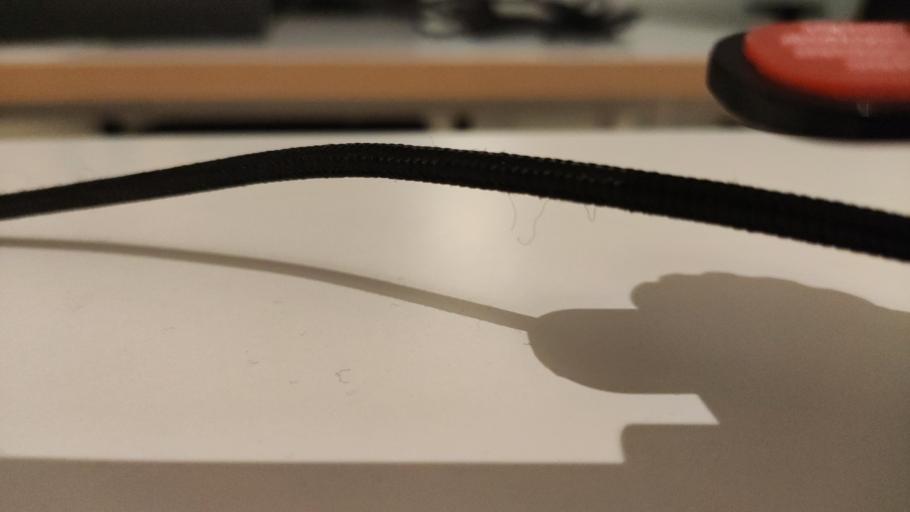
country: RU
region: Moskovskaya
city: Semkhoz
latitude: 56.4074
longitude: 38.0065
